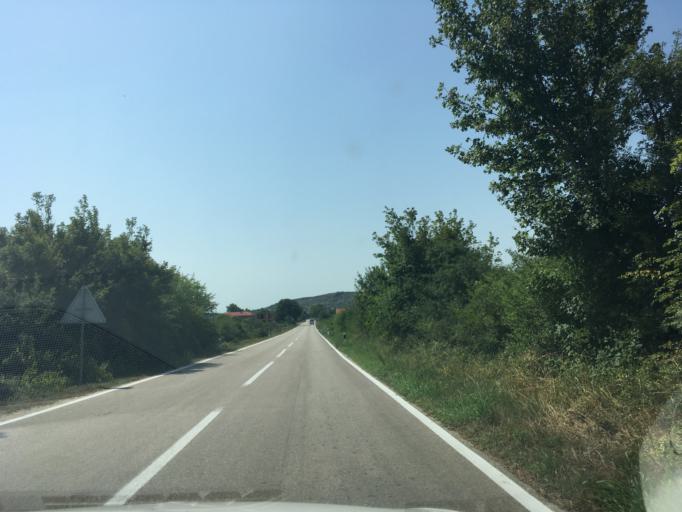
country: HR
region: Sibensko-Kniniska
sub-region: Grad Sibenik
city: Pirovac
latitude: 43.9598
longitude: 15.7710
